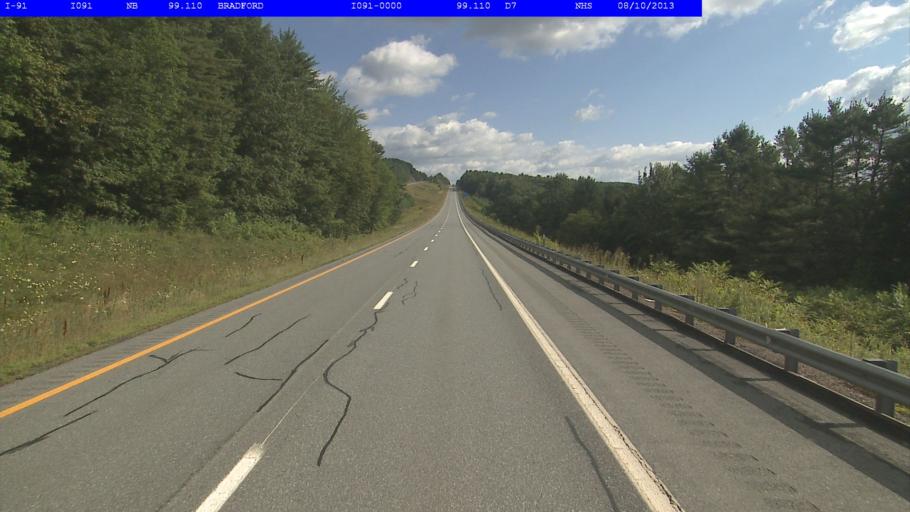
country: US
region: New Hampshire
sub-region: Grafton County
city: Haverhill
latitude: 44.0032
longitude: -72.1279
